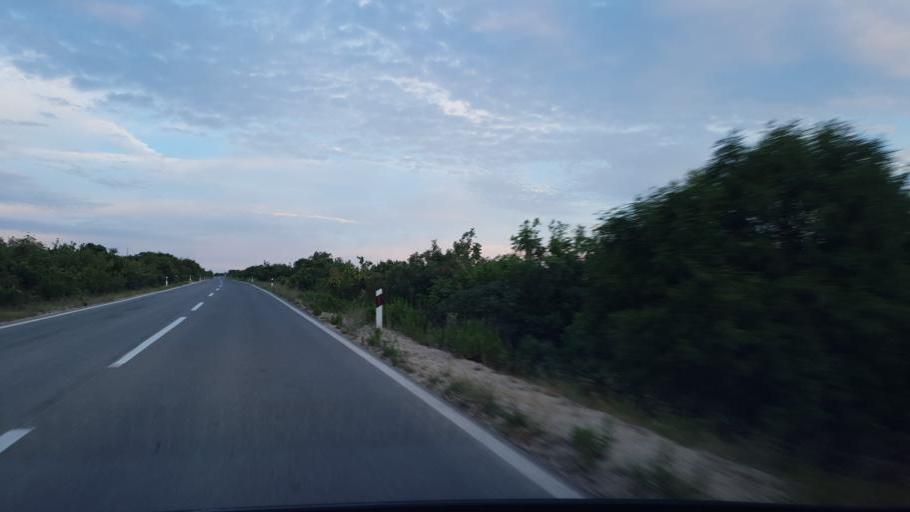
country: HR
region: Primorsko-Goranska
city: Punat
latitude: 45.0418
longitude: 14.6406
